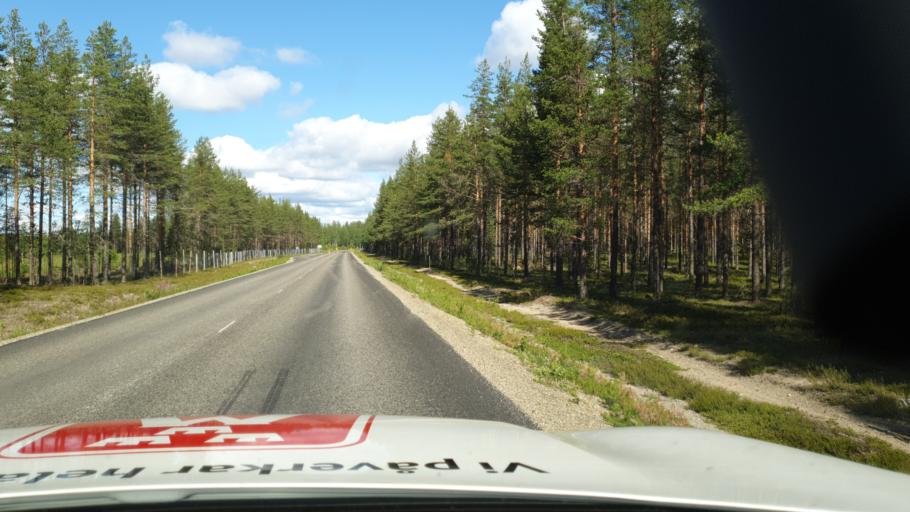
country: SE
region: Vaesterbotten
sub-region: Lycksele Kommun
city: Lycksele
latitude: 64.8282
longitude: 18.7907
